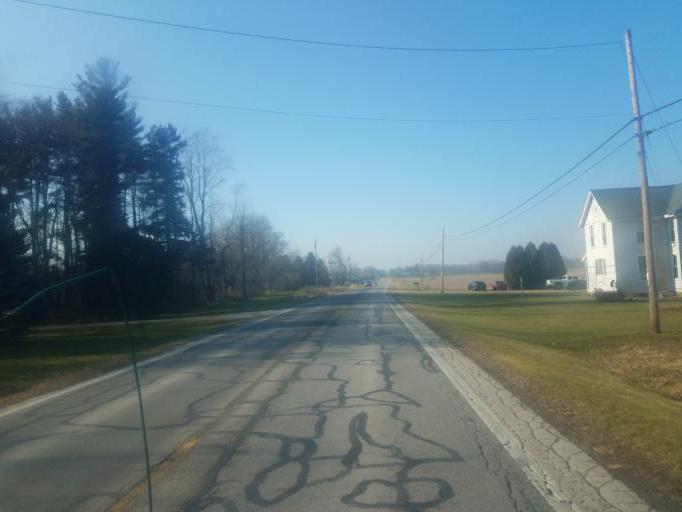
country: US
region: Ohio
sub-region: Seneca County
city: Tiffin
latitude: 41.1228
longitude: -83.1455
